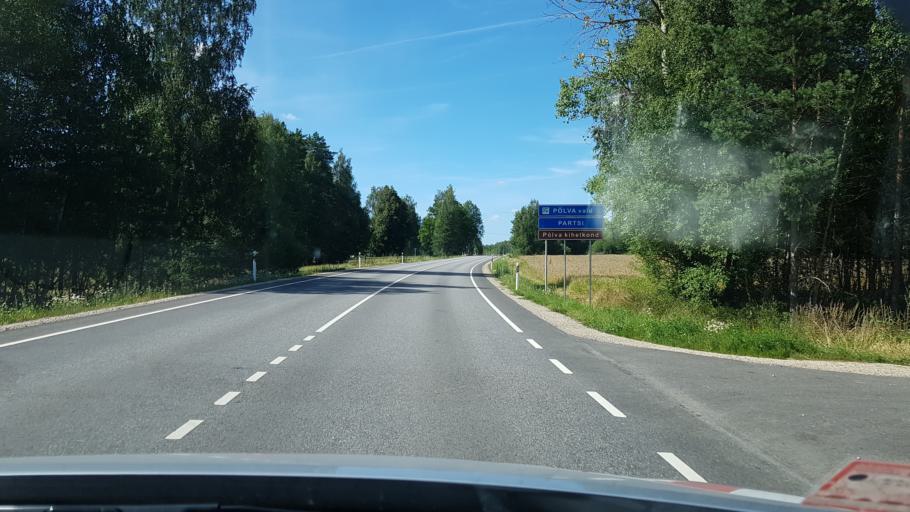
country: EE
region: Polvamaa
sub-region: Polva linn
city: Polva
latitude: 58.0041
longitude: 27.2102
